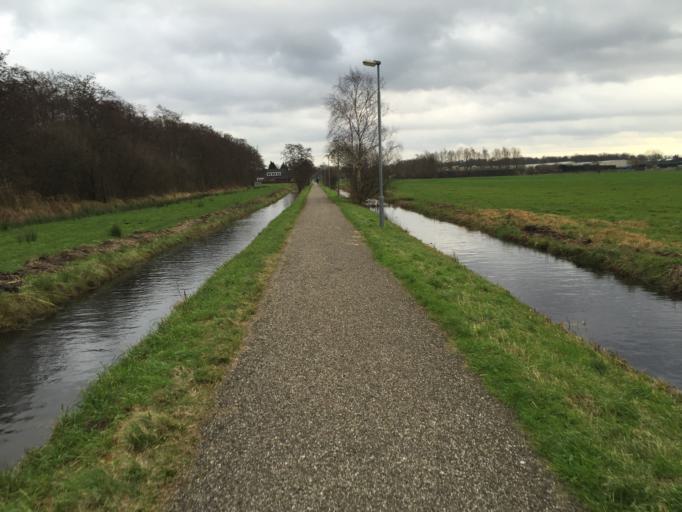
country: NL
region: North Holland
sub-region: Gemeente Wijdemeren
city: Kortenhoef
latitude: 52.2630
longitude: 5.1128
